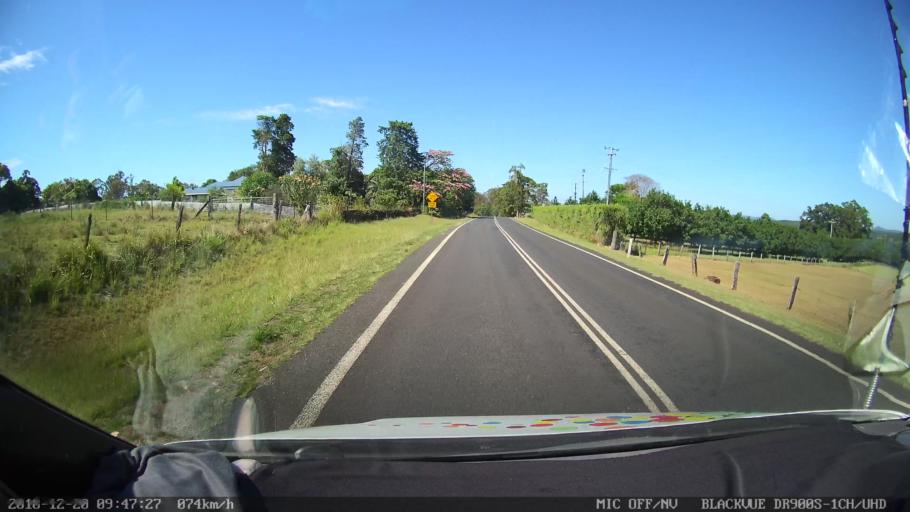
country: AU
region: New South Wales
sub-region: Lismore Municipality
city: Lismore
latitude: -28.7632
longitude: 153.2971
